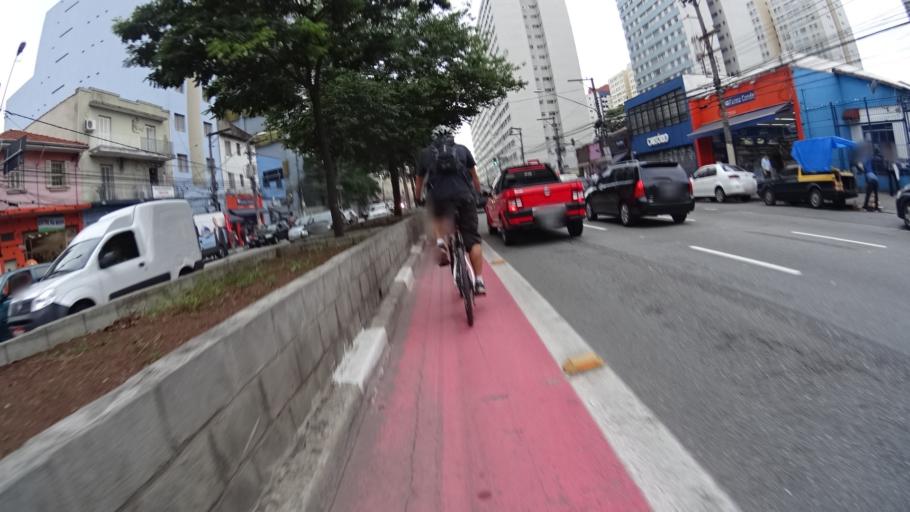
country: BR
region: Sao Paulo
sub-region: Diadema
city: Diadema
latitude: -23.6181
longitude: -46.6391
